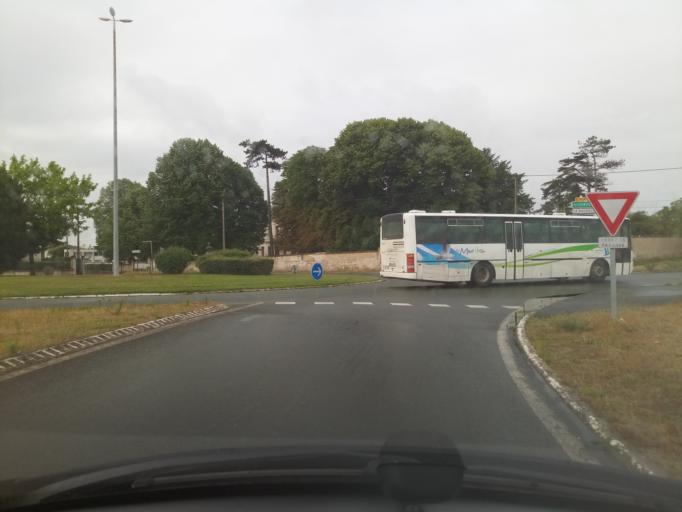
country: FR
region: Poitou-Charentes
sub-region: Departement de la Charente-Maritime
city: Surgeres
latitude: 46.1130
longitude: -0.7576
